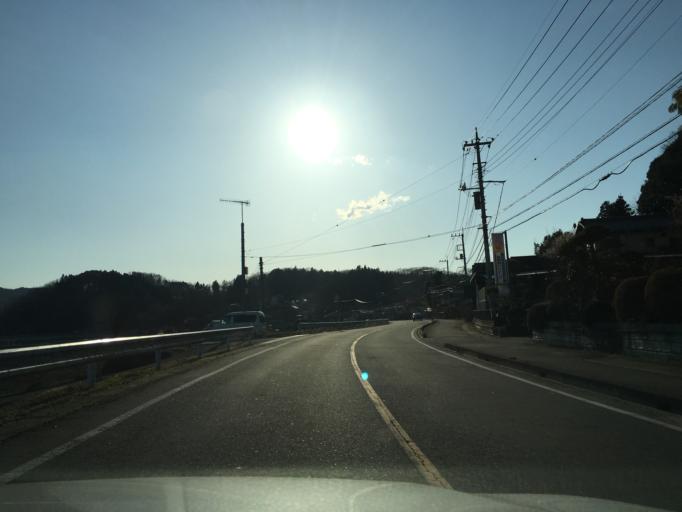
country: JP
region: Ibaraki
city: Daigo
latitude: 36.7829
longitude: 140.3103
